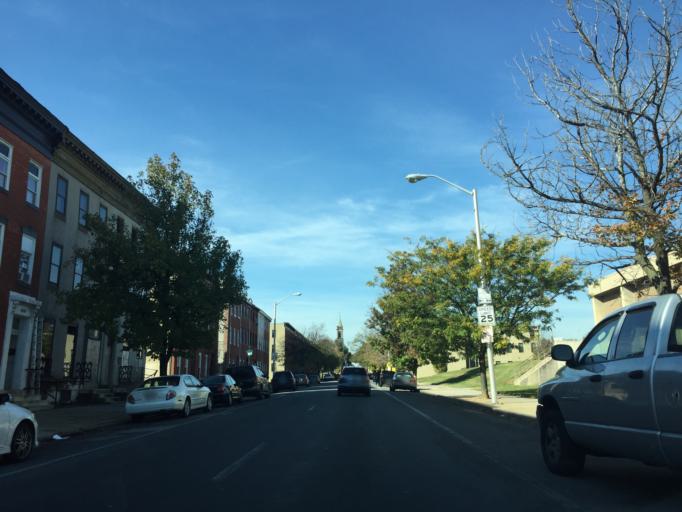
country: US
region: Maryland
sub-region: City of Baltimore
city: Baltimore
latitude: 39.2897
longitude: -76.6397
